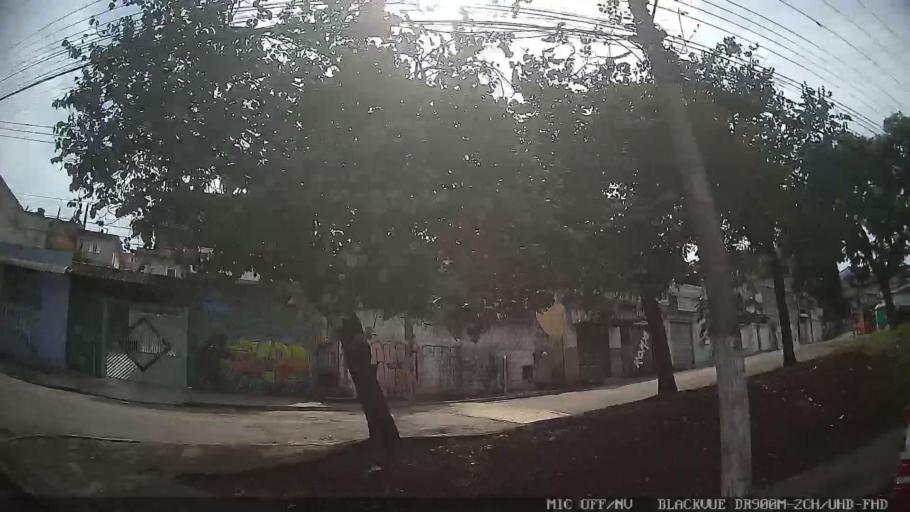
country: BR
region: Sao Paulo
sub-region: Suzano
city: Suzano
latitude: -23.5080
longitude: -46.3001
